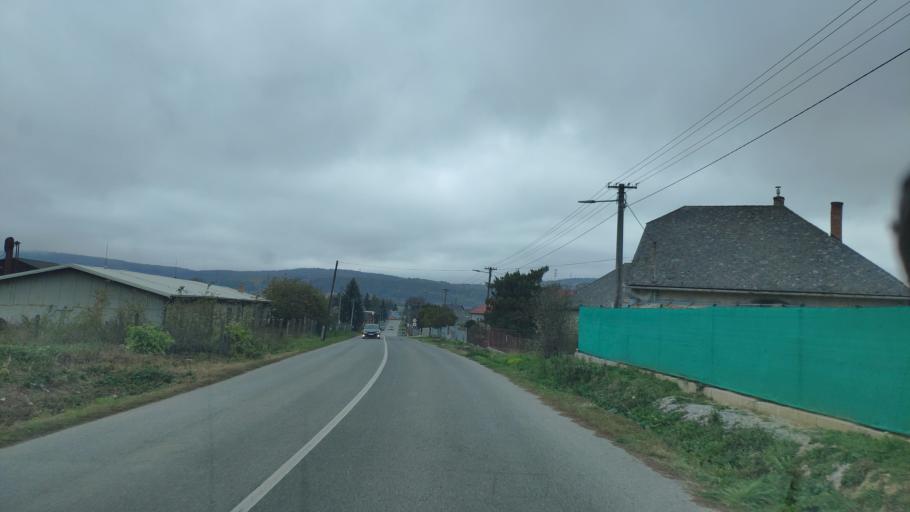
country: SK
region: Presovsky
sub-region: Okres Presov
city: Presov
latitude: 49.0164
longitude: 21.1870
